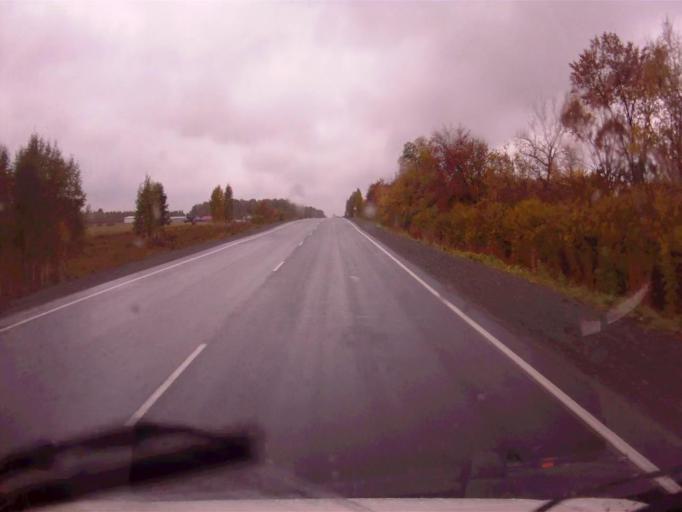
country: RU
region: Chelyabinsk
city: Novogornyy
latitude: 55.4890
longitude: 60.6931
